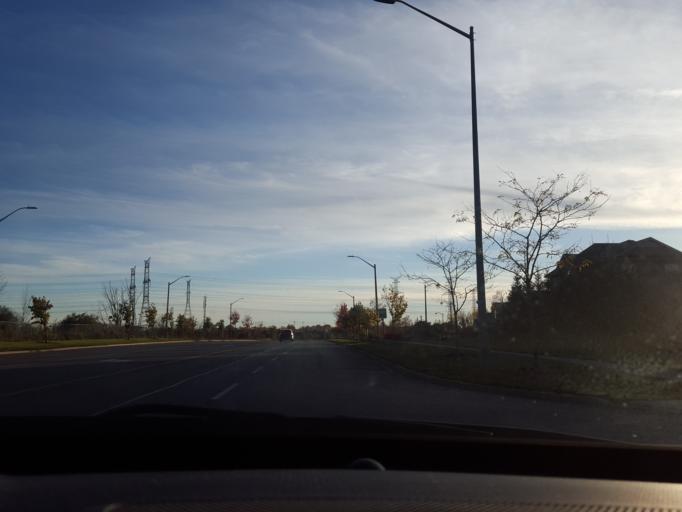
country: CA
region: Ontario
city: Markham
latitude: 43.8528
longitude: -79.2233
